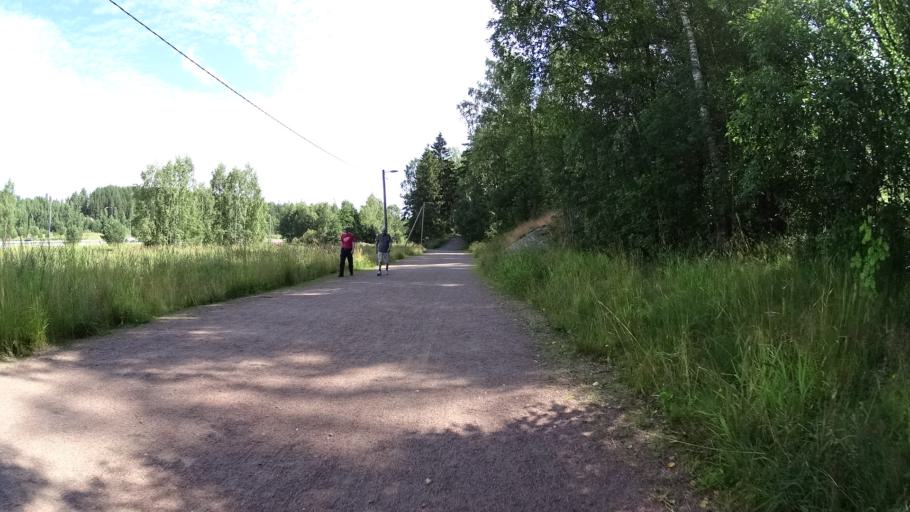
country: FI
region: Uusimaa
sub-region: Helsinki
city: Kirkkonummi
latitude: 60.1154
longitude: 24.4486
